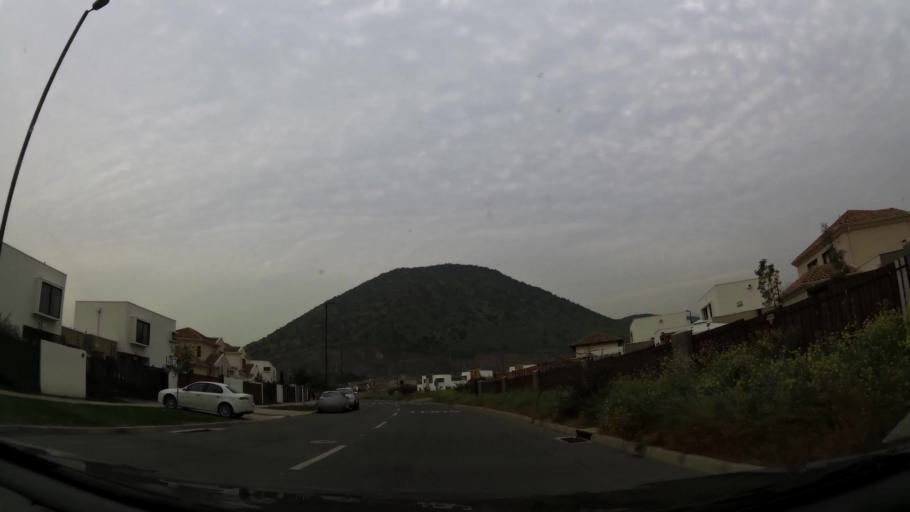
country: CL
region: Santiago Metropolitan
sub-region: Provincia de Chacabuco
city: Chicureo Abajo
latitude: -33.3146
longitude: -70.6535
